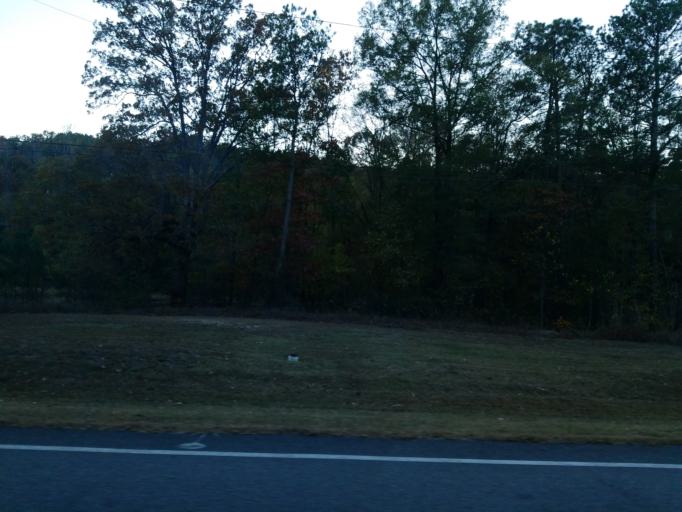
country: US
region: Georgia
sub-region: Gordon County
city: Calhoun
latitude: 34.5940
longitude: -85.0396
